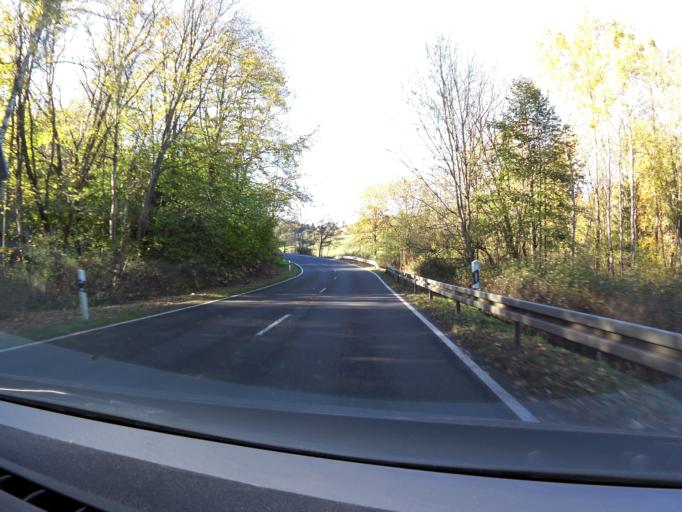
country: DE
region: Thuringia
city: Elgersburg
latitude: 50.7026
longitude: 10.8667
